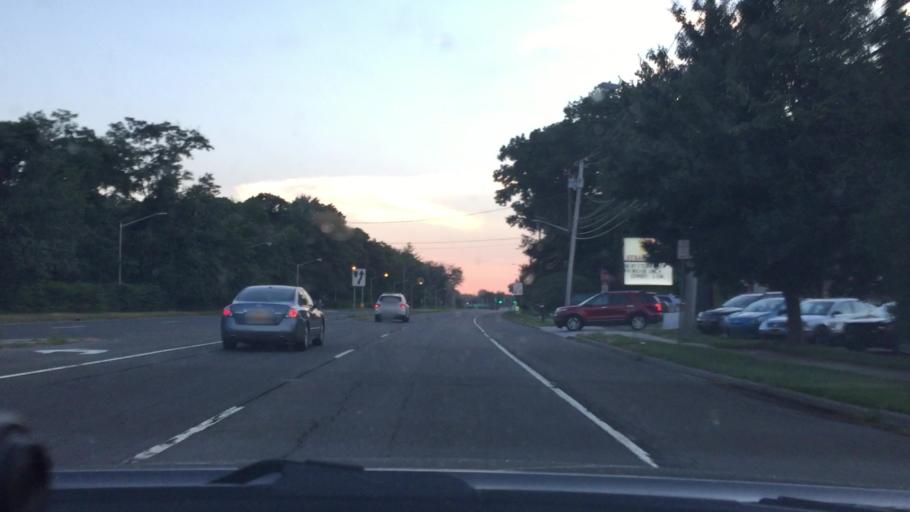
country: US
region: New York
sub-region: Suffolk County
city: Sound Beach
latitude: 40.9449
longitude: -72.9508
